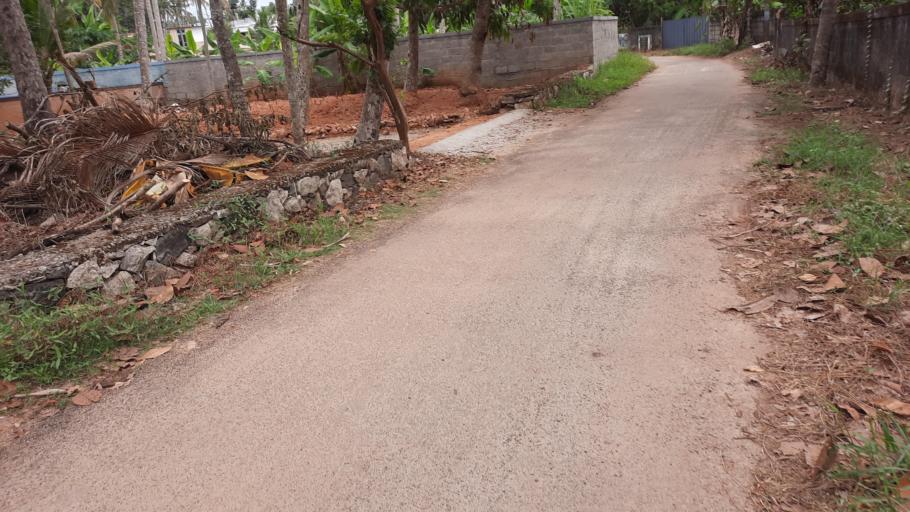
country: IN
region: Kerala
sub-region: Thiruvananthapuram
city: Thiruvananthapuram
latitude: 8.5601
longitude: 76.9314
